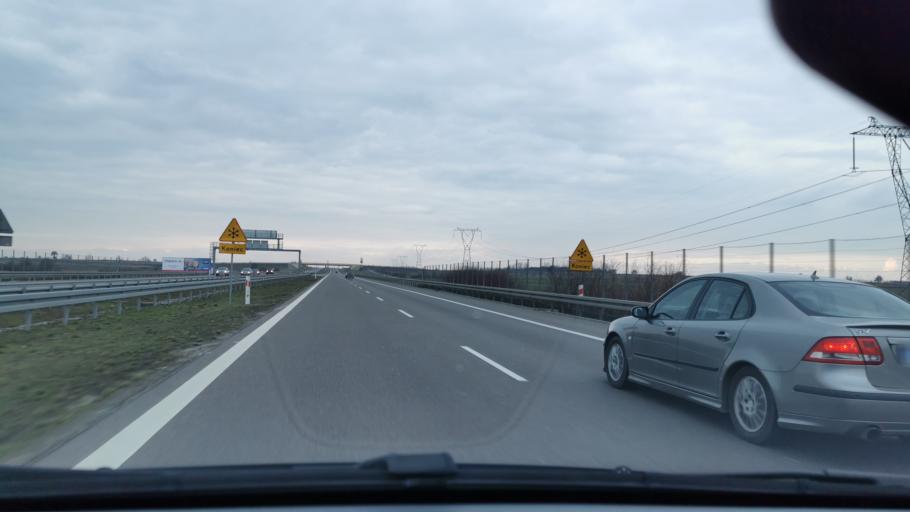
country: PL
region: Lublin Voivodeship
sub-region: Powiat pulawski
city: Markuszow
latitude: 51.3844
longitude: 22.2720
